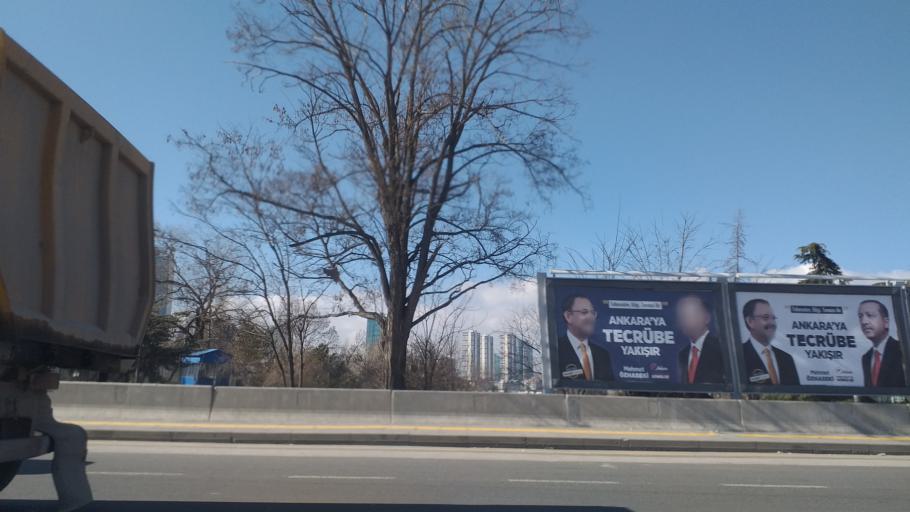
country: TR
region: Ankara
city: Ankara
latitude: 39.9159
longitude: 32.8140
